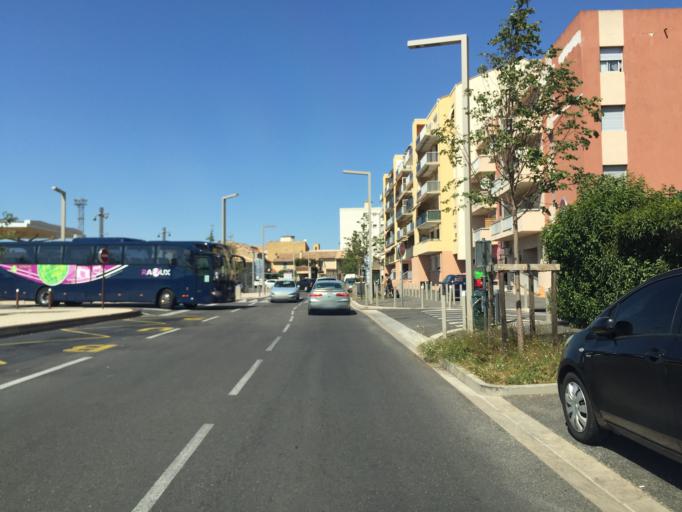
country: FR
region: Provence-Alpes-Cote d'Azur
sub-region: Departement du Vaucluse
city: Carpentras
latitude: 44.0483
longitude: 5.0454
